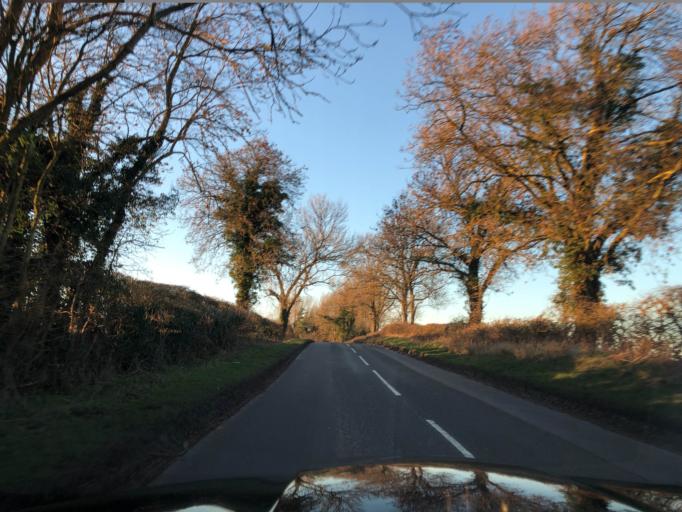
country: GB
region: England
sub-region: Warwickshire
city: Harbury
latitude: 52.2201
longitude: -1.4452
